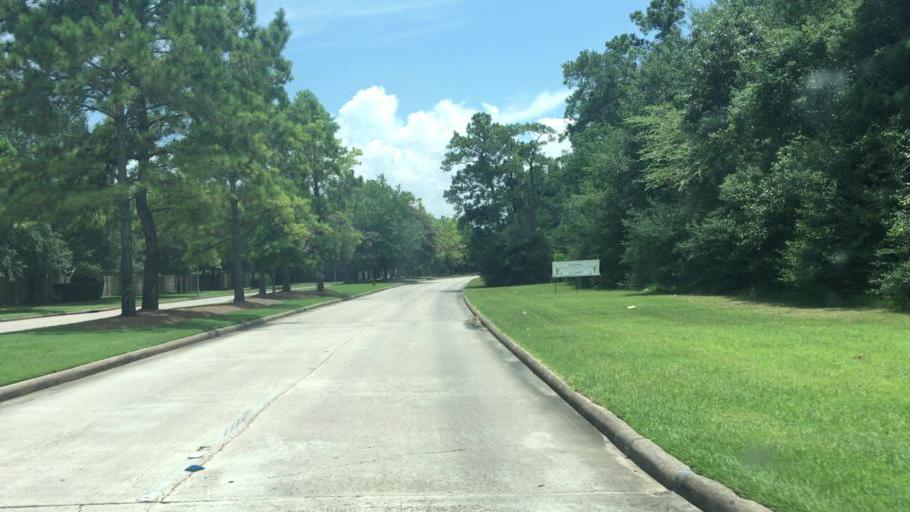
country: US
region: Texas
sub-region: Harris County
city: Atascocita
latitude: 29.9854
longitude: -95.1914
